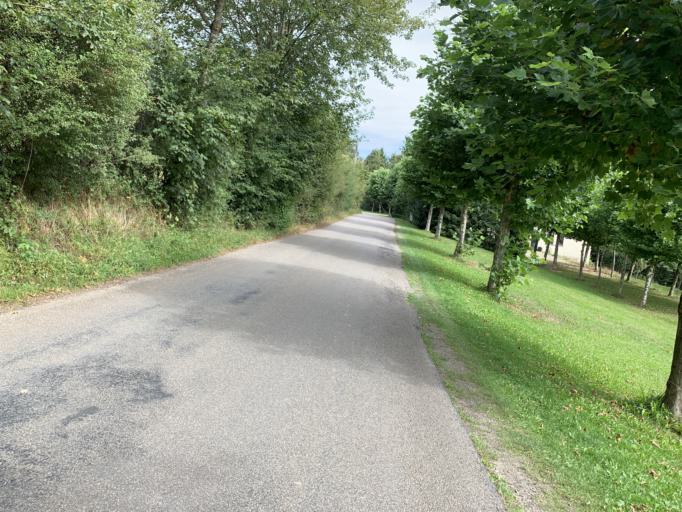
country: BE
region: Wallonia
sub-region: Province du Luxembourg
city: Tellin
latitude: 50.0952
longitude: 5.2808
